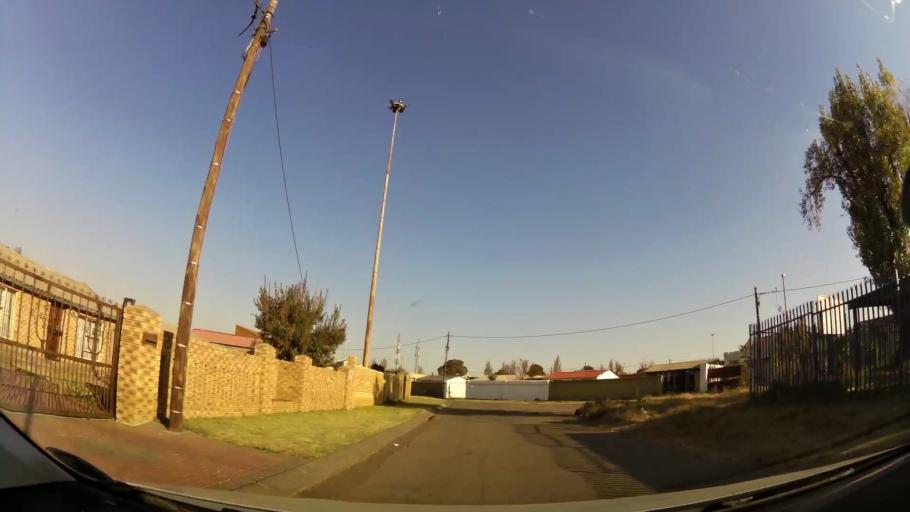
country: ZA
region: Gauteng
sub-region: City of Johannesburg Metropolitan Municipality
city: Soweto
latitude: -26.2665
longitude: 27.8751
